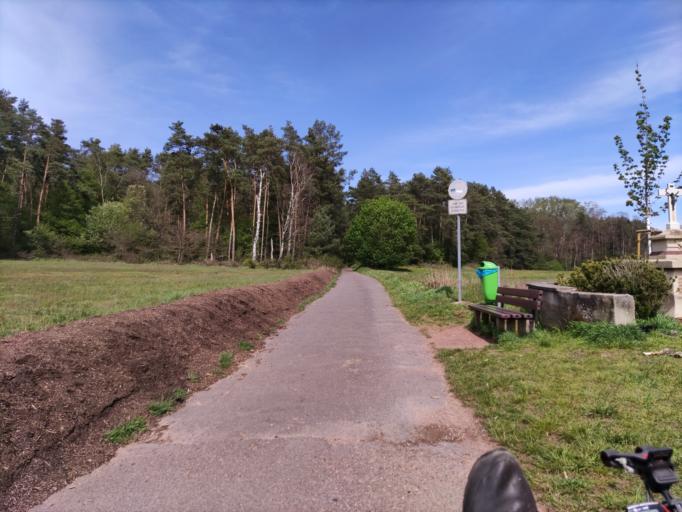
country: DE
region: Saarland
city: Saarlouis
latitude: 49.3415
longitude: 6.7704
